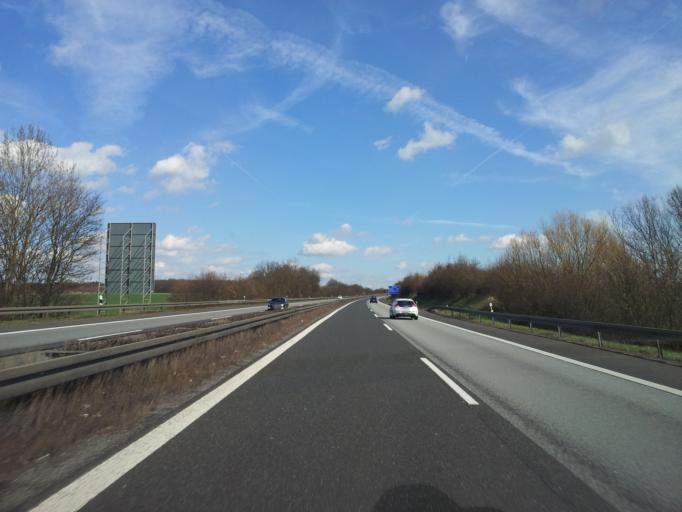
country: DE
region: Bavaria
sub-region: Regierungsbezirk Unterfranken
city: Gochsheim
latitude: 50.0307
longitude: 10.2745
